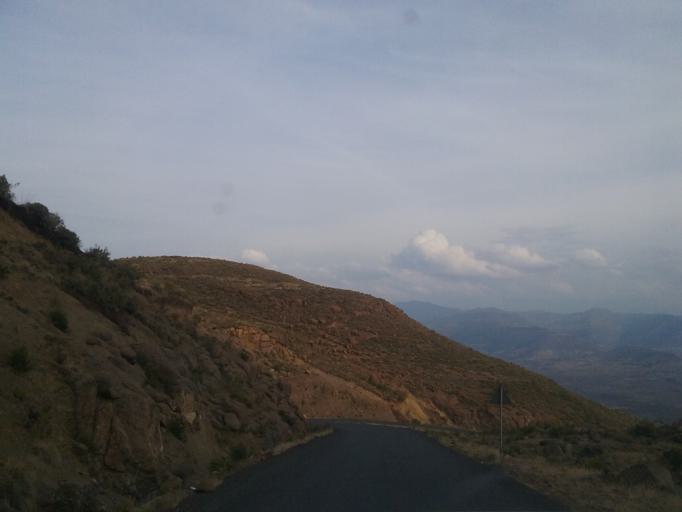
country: LS
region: Quthing
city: Quthing
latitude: -30.1932
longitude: 27.9711
